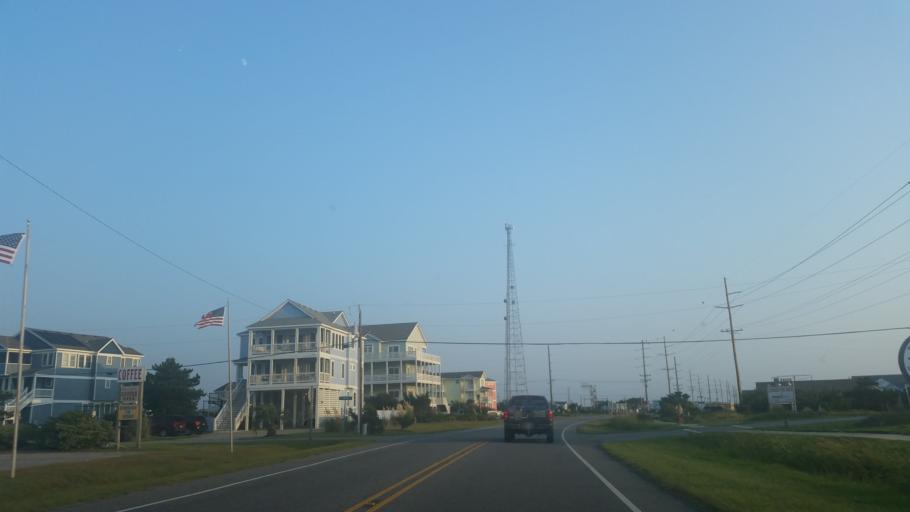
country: US
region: North Carolina
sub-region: Dare County
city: Wanchese
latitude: 35.5868
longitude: -75.4676
